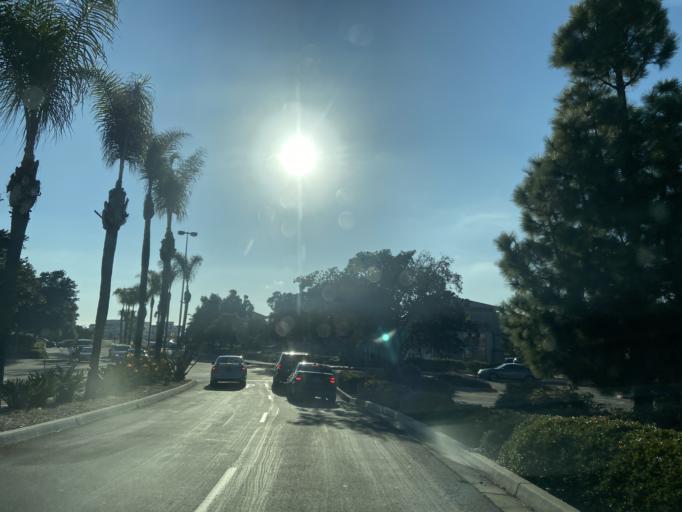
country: US
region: California
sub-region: San Diego County
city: Bonita
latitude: 32.6302
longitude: -116.9661
